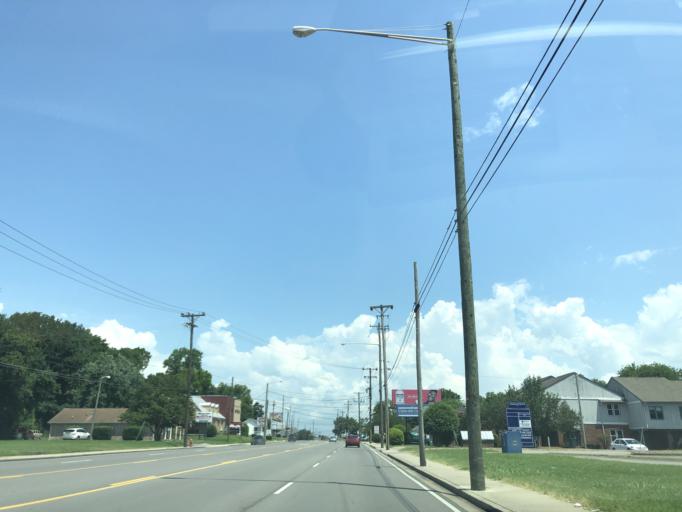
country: US
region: Tennessee
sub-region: Davidson County
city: Lakewood
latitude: 36.1611
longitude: -86.6642
